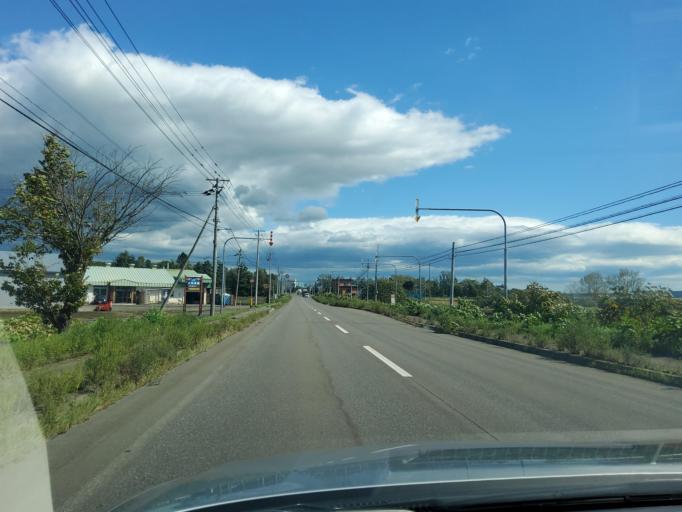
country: JP
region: Hokkaido
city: Obihiro
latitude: 42.9360
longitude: 143.2912
